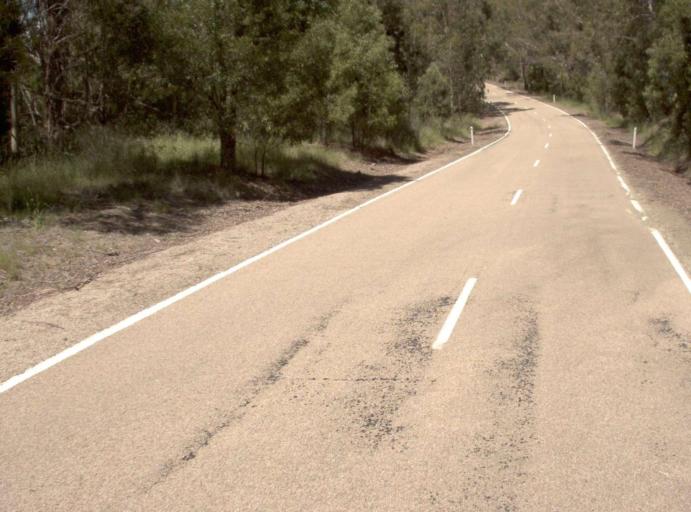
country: AU
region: Victoria
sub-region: East Gippsland
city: Lakes Entrance
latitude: -37.2159
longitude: 148.2676
